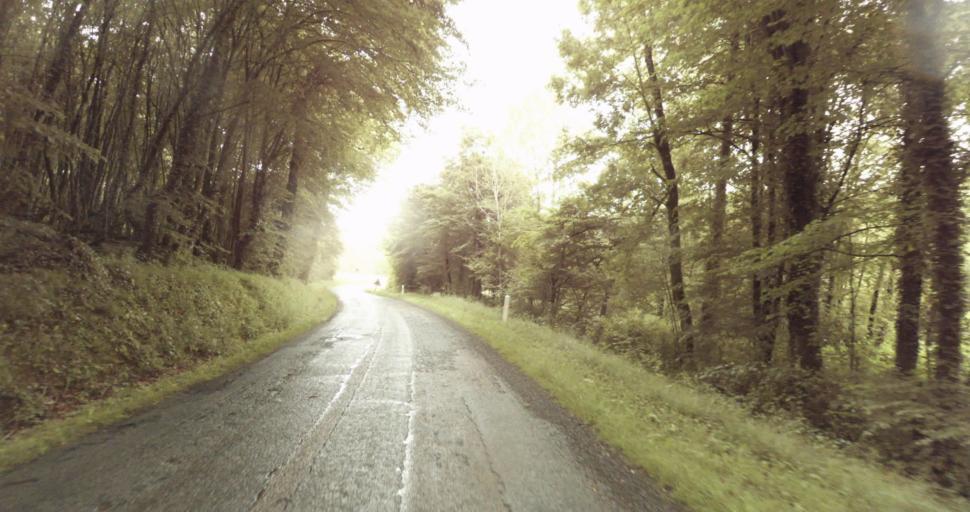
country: FR
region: Aquitaine
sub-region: Departement de la Dordogne
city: Belves
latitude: 44.7540
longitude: 0.9403
